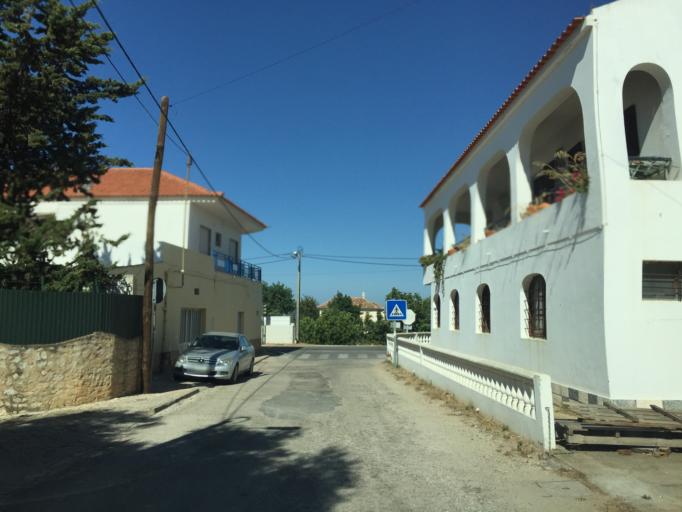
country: PT
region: Faro
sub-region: Loule
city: Almancil
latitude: 37.1005
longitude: -8.0417
